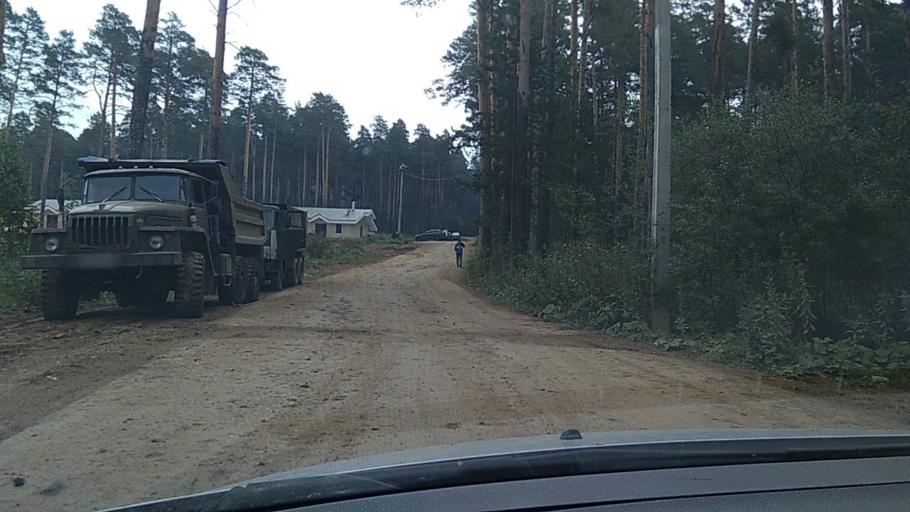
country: RU
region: Chelyabinsk
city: Zlatoust
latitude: 55.1602
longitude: 59.7012
